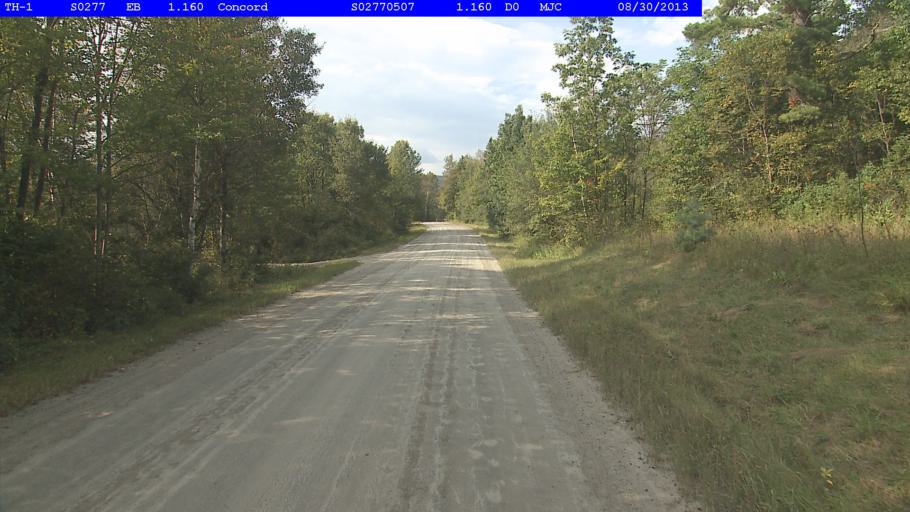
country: US
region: Vermont
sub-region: Caledonia County
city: Lyndonville
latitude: 44.4801
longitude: -71.8638
